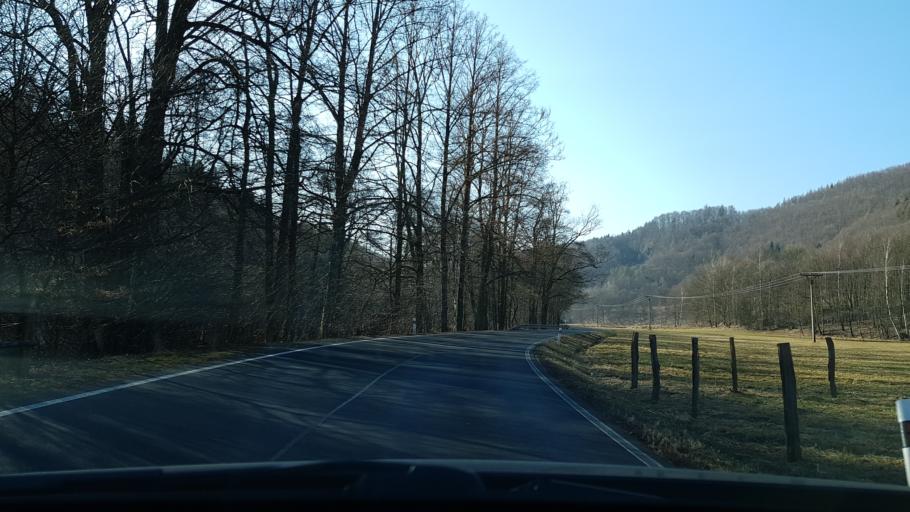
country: CZ
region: Olomoucky
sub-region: Okres Sumperk
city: Hanusovice
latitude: 50.0525
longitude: 16.9175
